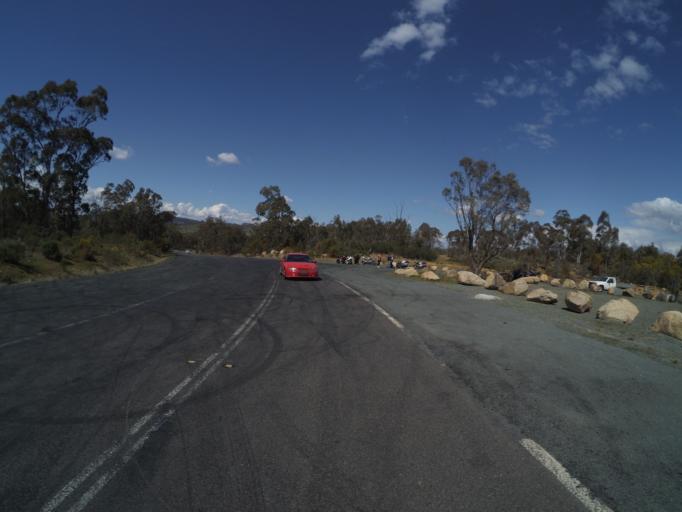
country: AU
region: Australian Capital Territory
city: Macquarie
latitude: -35.3137
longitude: 148.9479
